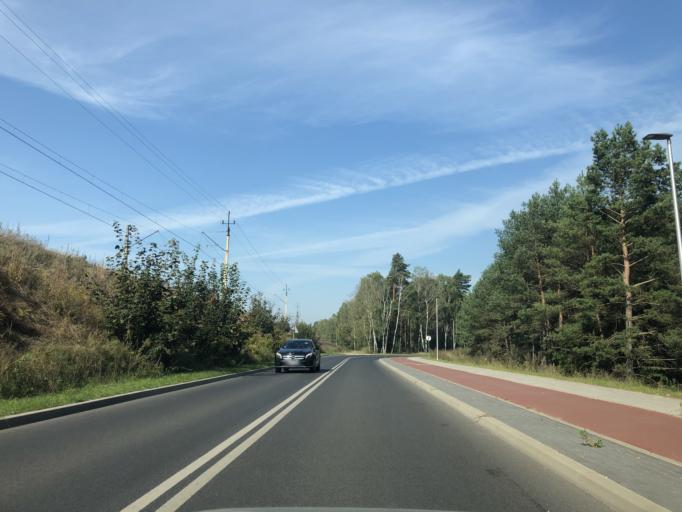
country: PL
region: Greater Poland Voivodeship
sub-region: Powiat pilski
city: Pila
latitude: 53.1344
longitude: 16.7961
